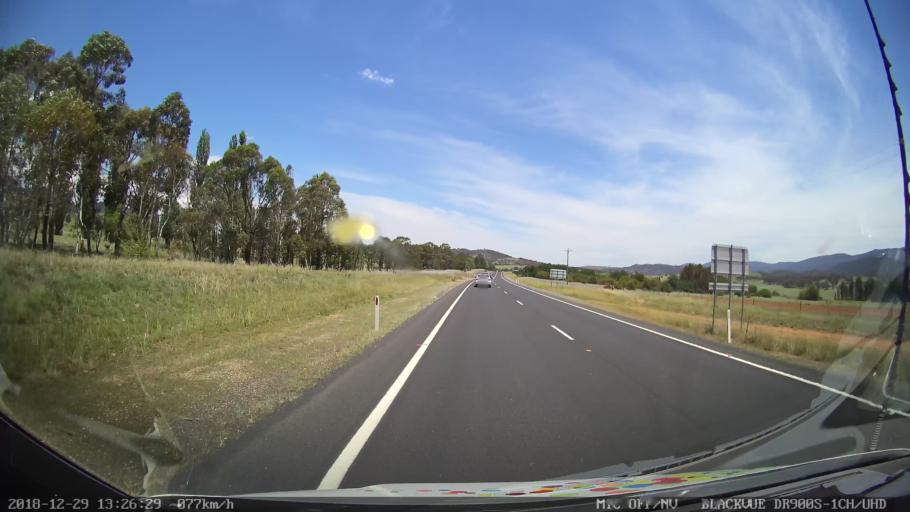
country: AU
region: New South Wales
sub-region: Cooma-Monaro
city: Cooma
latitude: -35.8559
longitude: 149.1590
